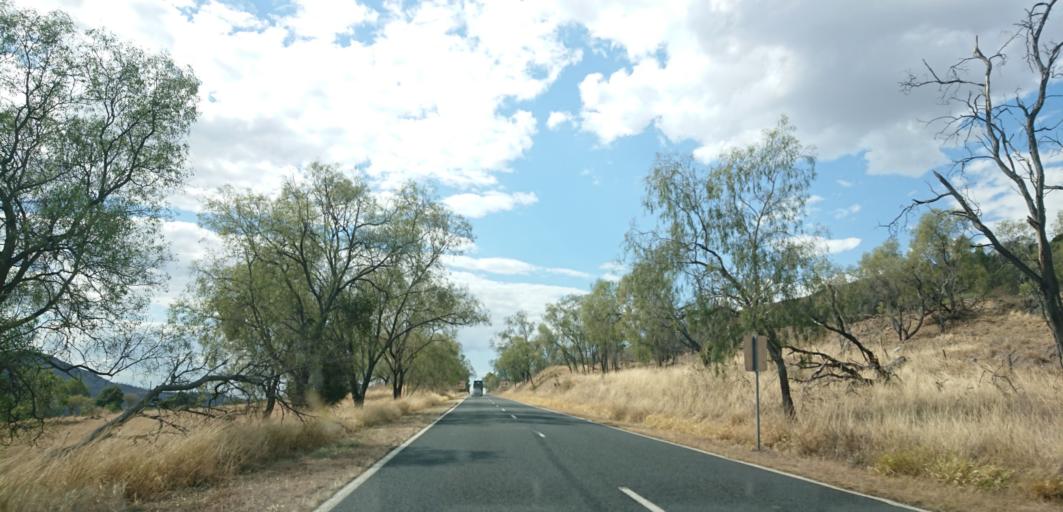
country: AU
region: Queensland
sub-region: Lockyer Valley
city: Gatton
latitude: -27.6848
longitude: 152.1474
